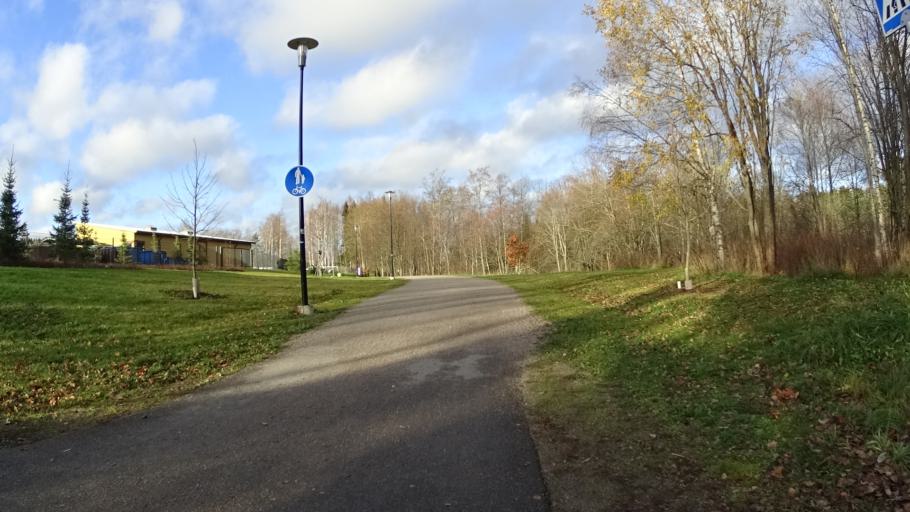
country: FI
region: Uusimaa
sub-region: Helsinki
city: Vantaa
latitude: 60.3017
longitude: 25.0168
